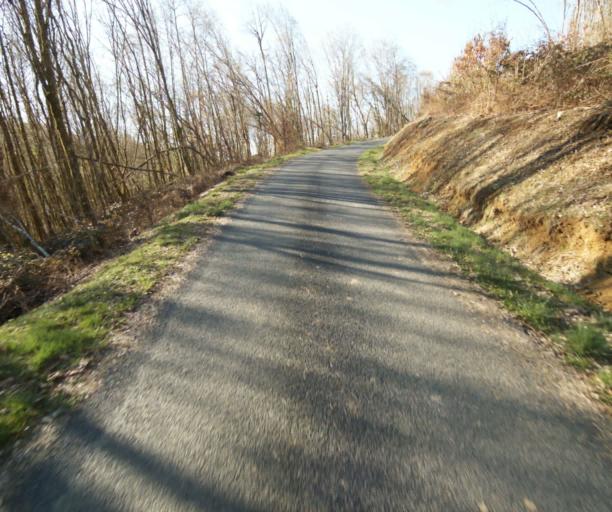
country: FR
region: Limousin
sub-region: Departement de la Correze
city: Seilhac
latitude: 45.3769
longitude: 1.7701
